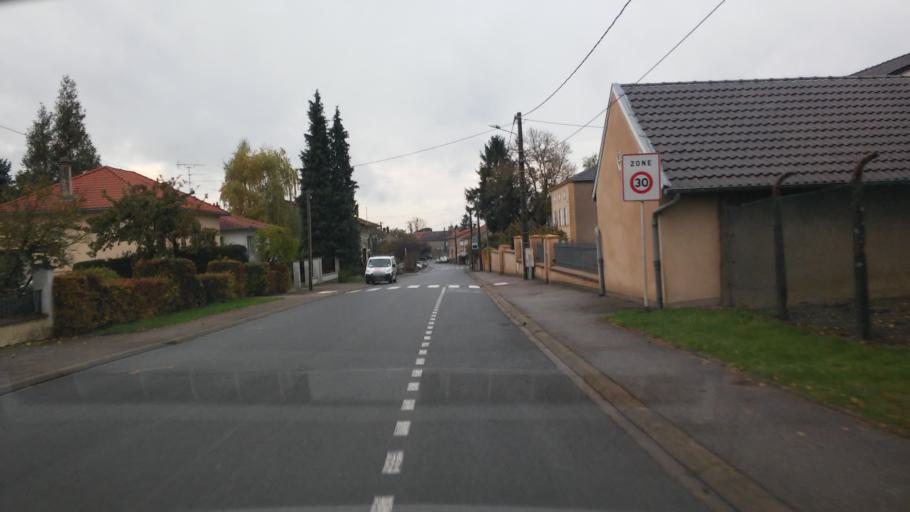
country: FR
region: Lorraine
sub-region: Departement de la Moselle
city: Vigy
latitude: 49.2006
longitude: 6.2995
